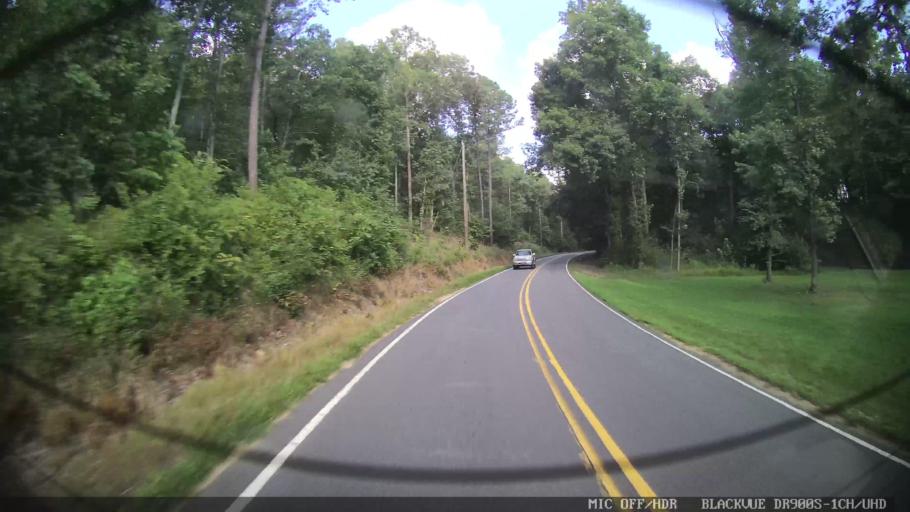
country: US
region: Georgia
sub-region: Floyd County
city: Lindale
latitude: 34.1956
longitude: -85.0667
